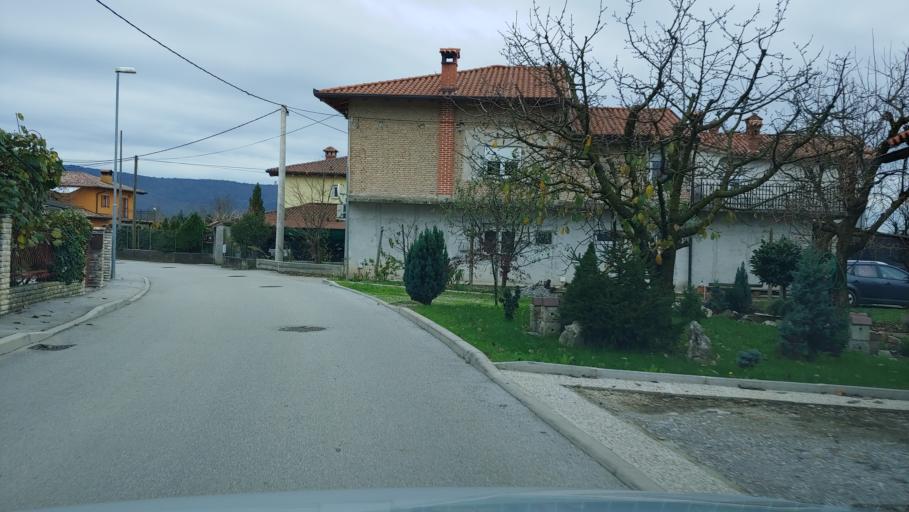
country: SI
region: Sempeter-Vrtojba
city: Vrtojba
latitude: 45.9128
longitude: 13.6299
